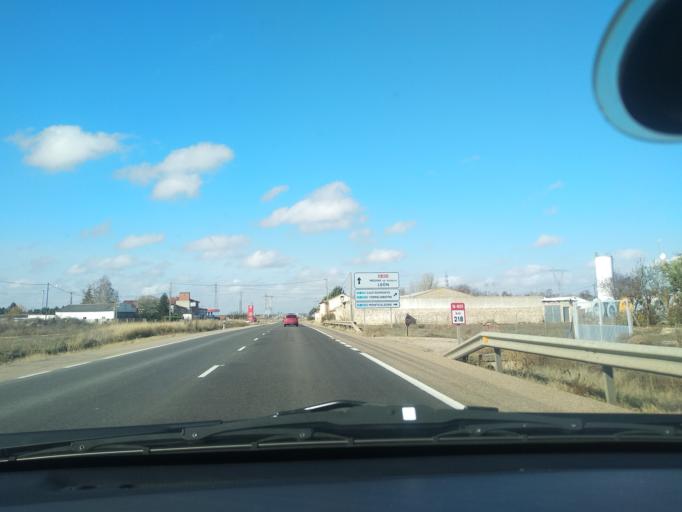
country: ES
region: Castille and Leon
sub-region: Provincia de Valladolid
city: Valdenebro de los Valles
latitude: 41.7849
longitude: -4.9396
